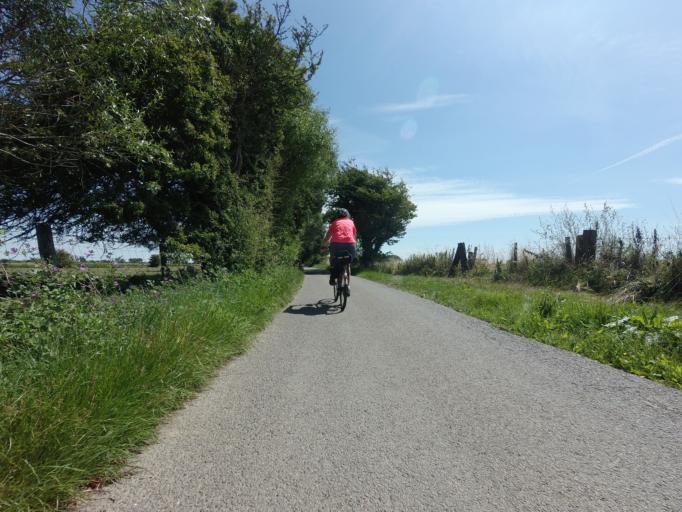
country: GB
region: England
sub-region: Kent
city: Lydd
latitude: 50.9853
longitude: 0.8740
